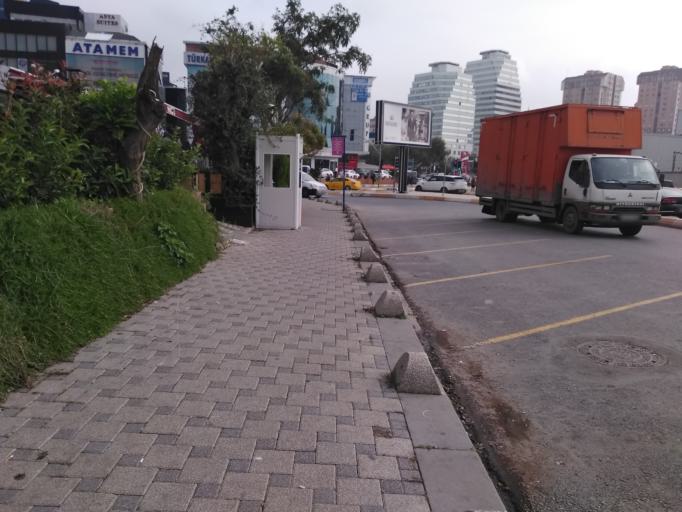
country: TR
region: Istanbul
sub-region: Atasehir
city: Atasehir
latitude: 40.9801
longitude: 29.1031
